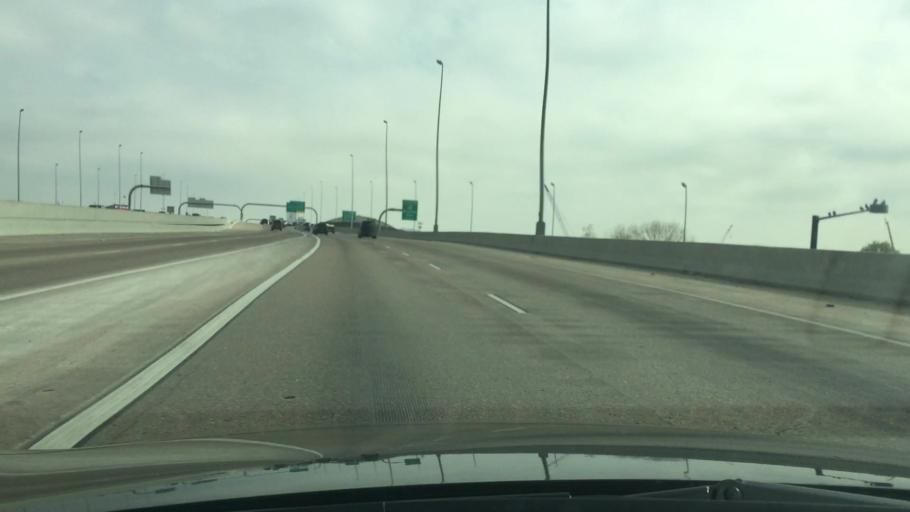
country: US
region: Colorado
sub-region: Denver County
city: Denver
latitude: 39.7794
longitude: -104.9794
